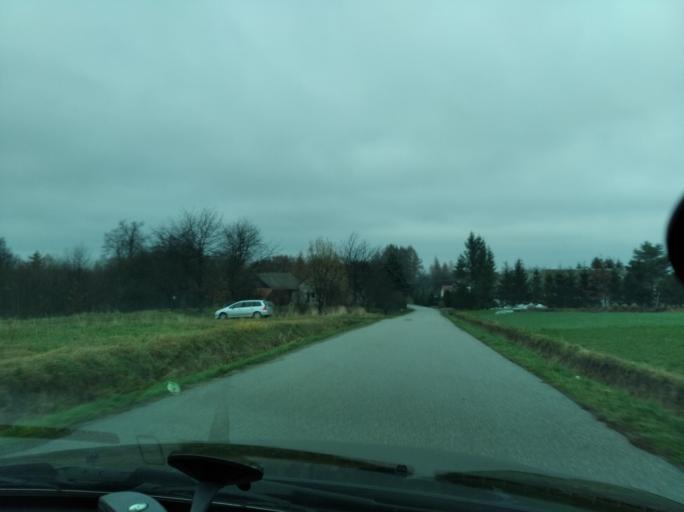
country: PL
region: Subcarpathian Voivodeship
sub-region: Powiat przeworski
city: Jawornik Polski
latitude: 49.8988
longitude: 22.2768
